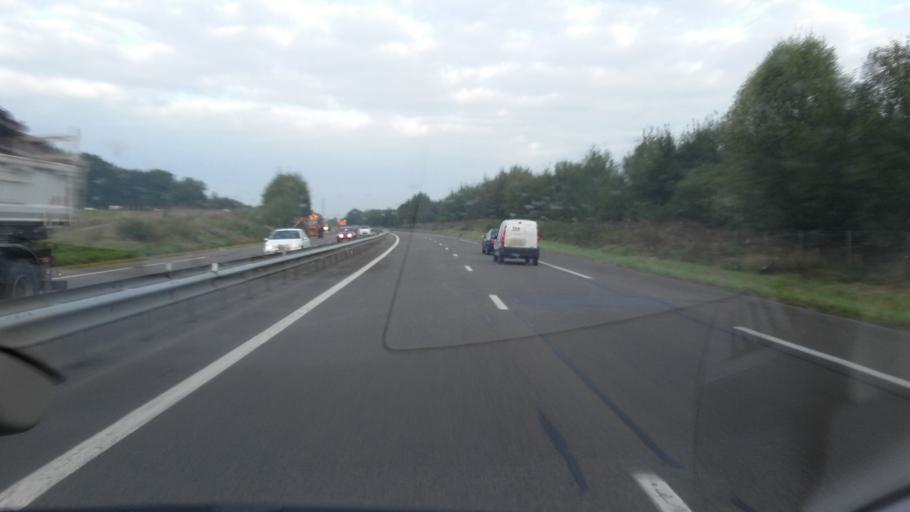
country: FR
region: Champagne-Ardenne
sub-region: Departement des Ardennes
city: La Francheville
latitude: 49.6435
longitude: 4.5922
